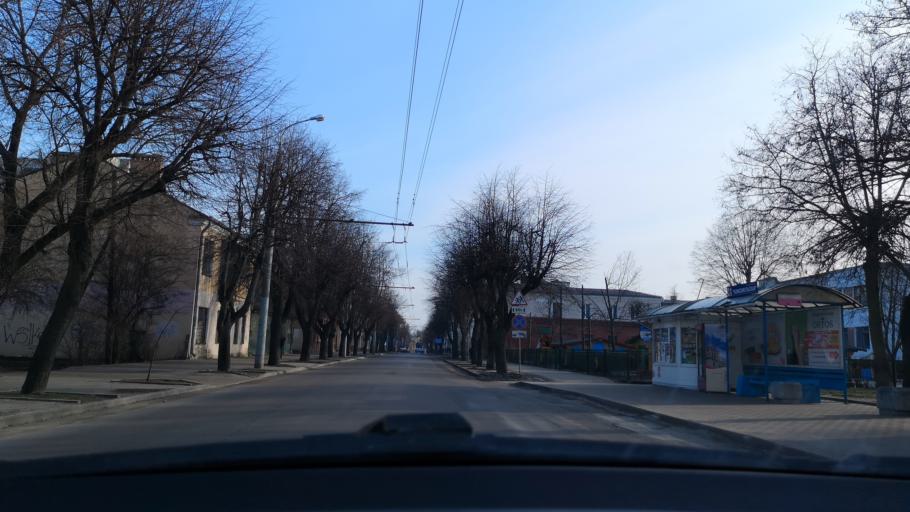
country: BY
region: Brest
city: Brest
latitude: 52.0965
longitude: 23.6868
